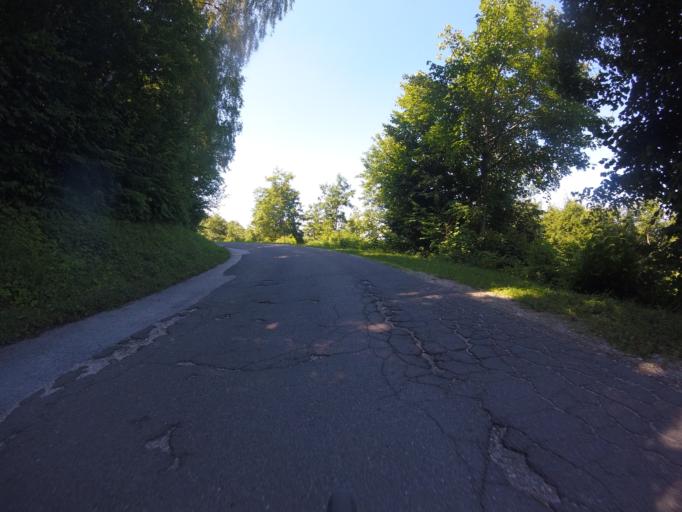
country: SI
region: Kostanjevica na Krki
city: Kostanjevica na Krki
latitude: 45.8026
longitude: 15.4966
